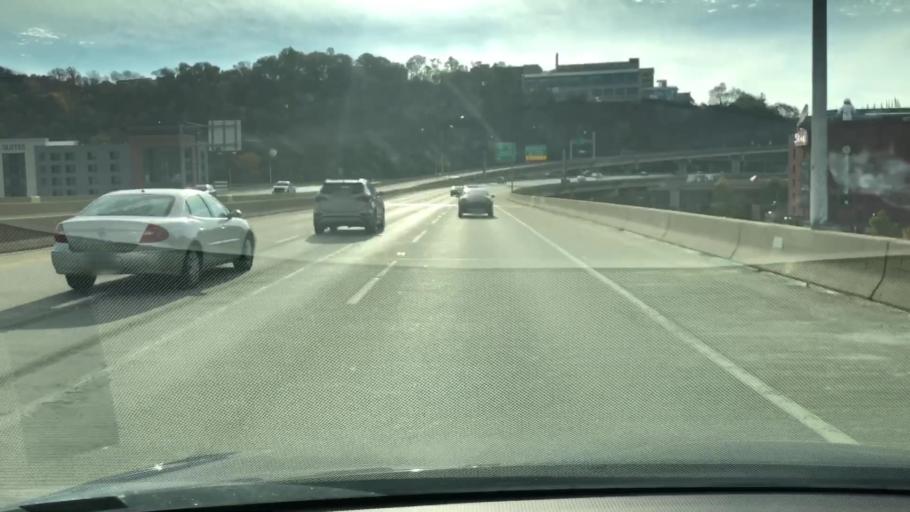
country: US
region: Pennsylvania
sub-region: Allegheny County
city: Pittsburgh
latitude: 40.4488
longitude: -79.9925
